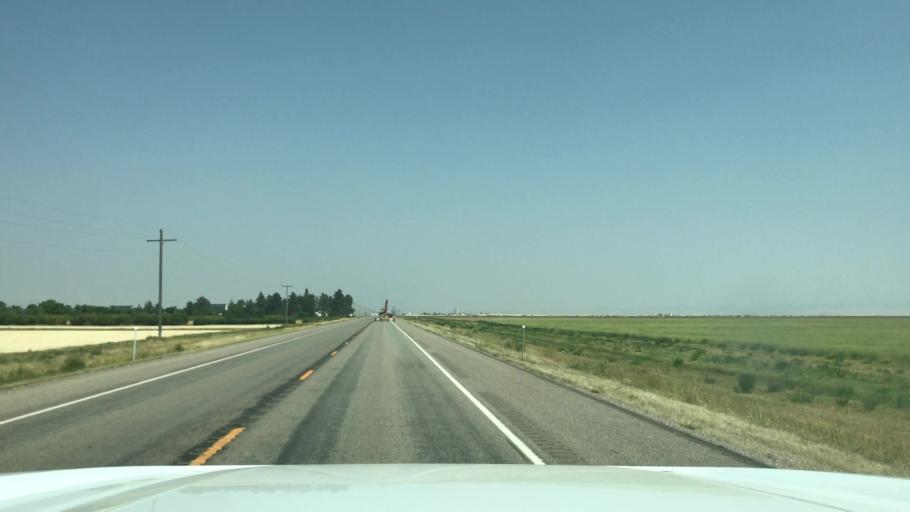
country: US
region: Montana
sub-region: Judith Basin County
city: Stanford
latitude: 47.0551
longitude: -109.9602
